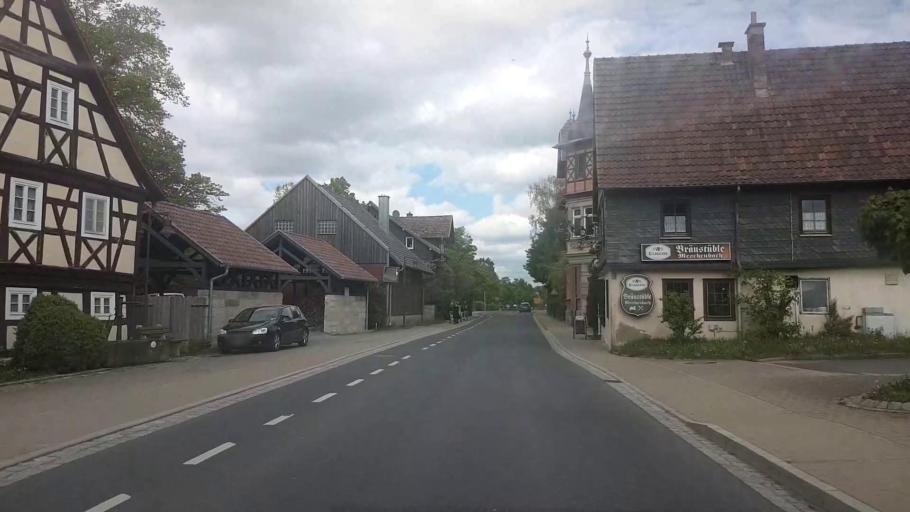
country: DE
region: Bavaria
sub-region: Upper Franconia
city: Untersiemau
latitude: 50.2058
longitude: 10.9753
